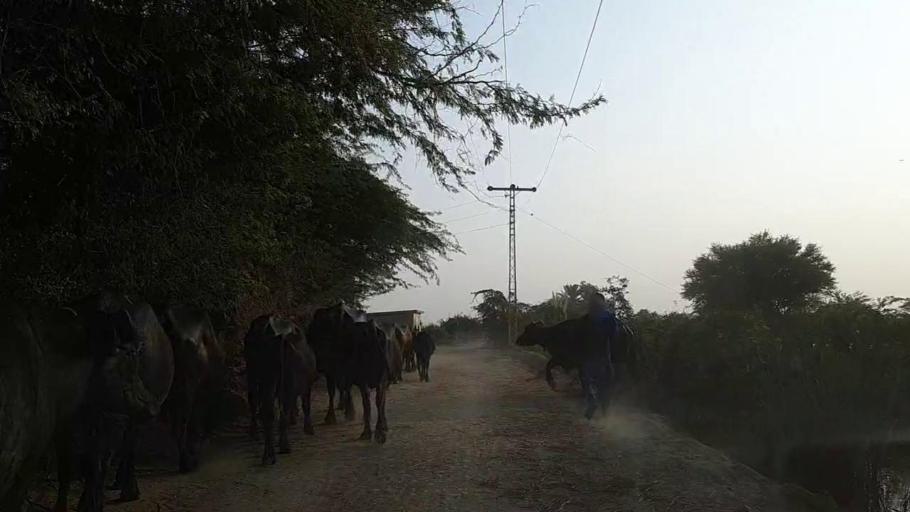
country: PK
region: Sindh
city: Thatta
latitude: 24.6908
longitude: 67.8090
